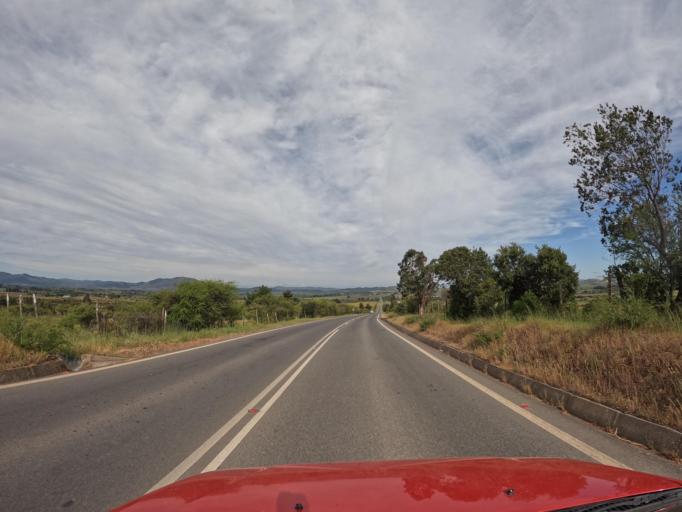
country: CL
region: Maule
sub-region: Provincia de Talca
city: Talca
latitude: -35.3689
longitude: -71.8480
